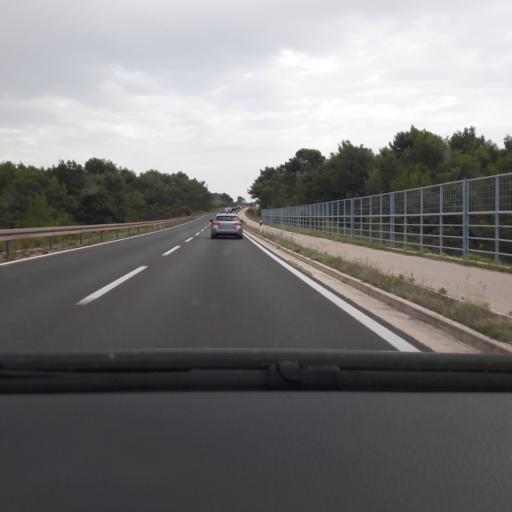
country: HR
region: Zadarska
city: Nin
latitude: 44.1826
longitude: 15.1863
